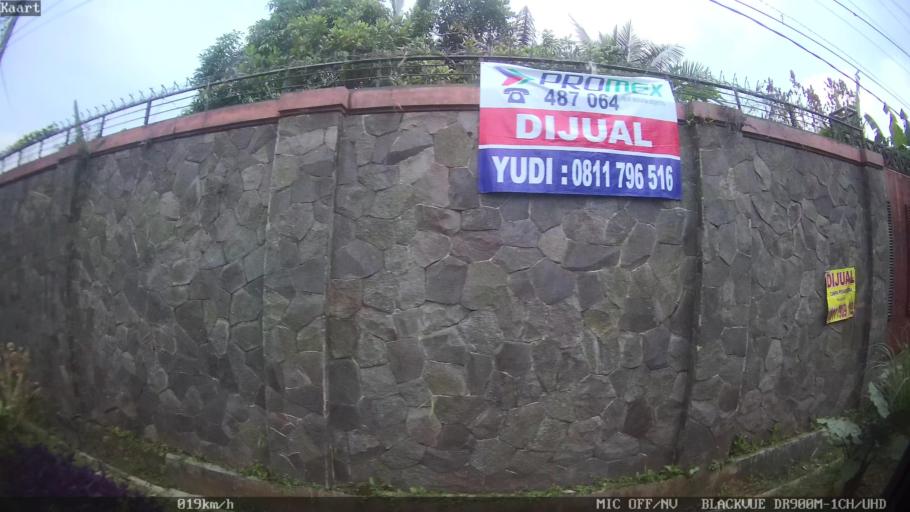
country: ID
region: Lampung
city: Bandarlampung
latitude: -5.4241
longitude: 105.2606
